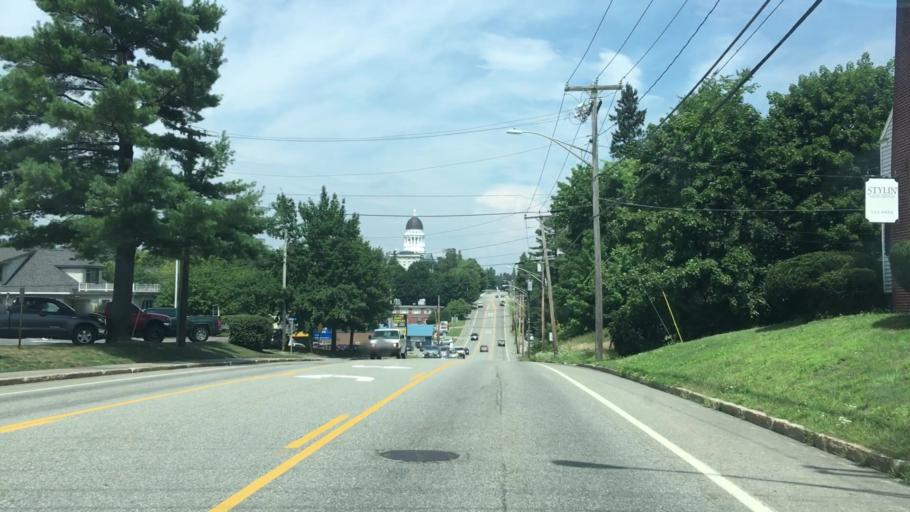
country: US
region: Maine
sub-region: Kennebec County
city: Augusta
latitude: 44.3008
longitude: -69.7825
